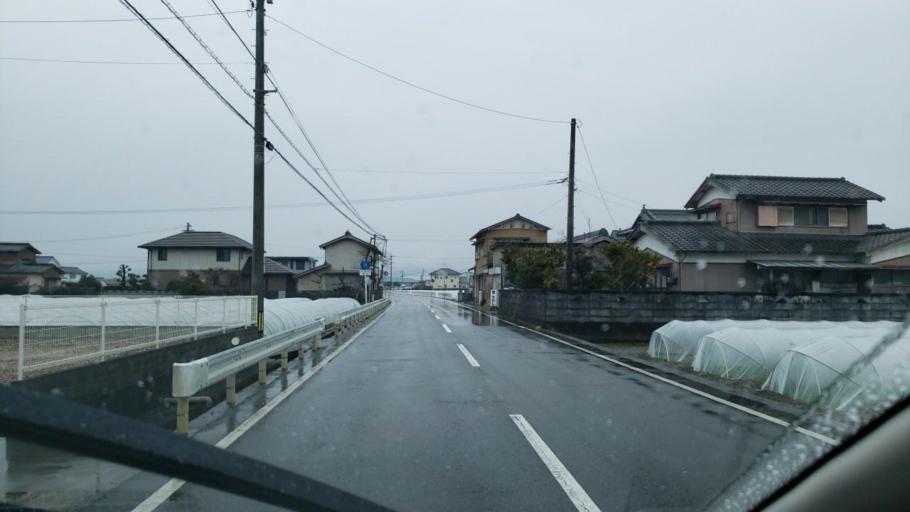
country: JP
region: Tokushima
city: Ishii
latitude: 34.1016
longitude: 134.4069
